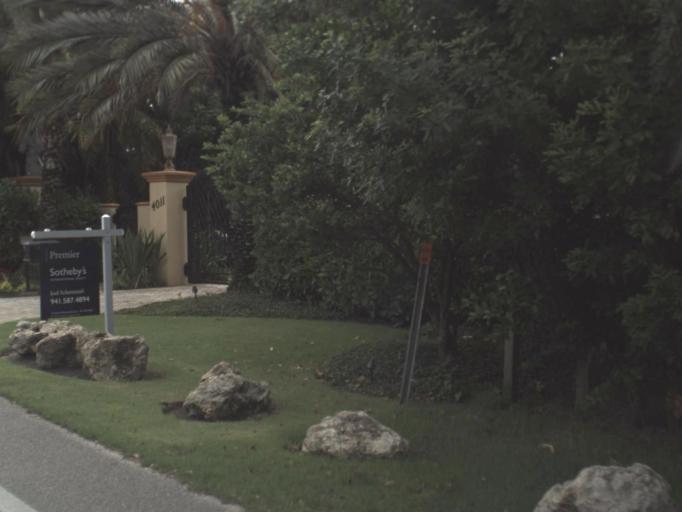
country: US
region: Florida
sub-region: Sarasota County
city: Siesta Key
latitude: 27.2973
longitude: -82.5582
